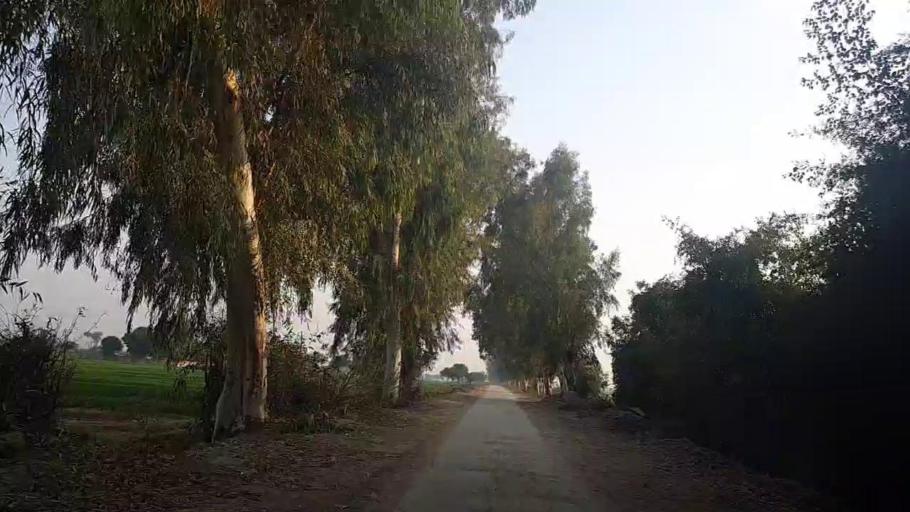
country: PK
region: Sindh
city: Sakrand
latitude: 26.1308
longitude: 68.2288
